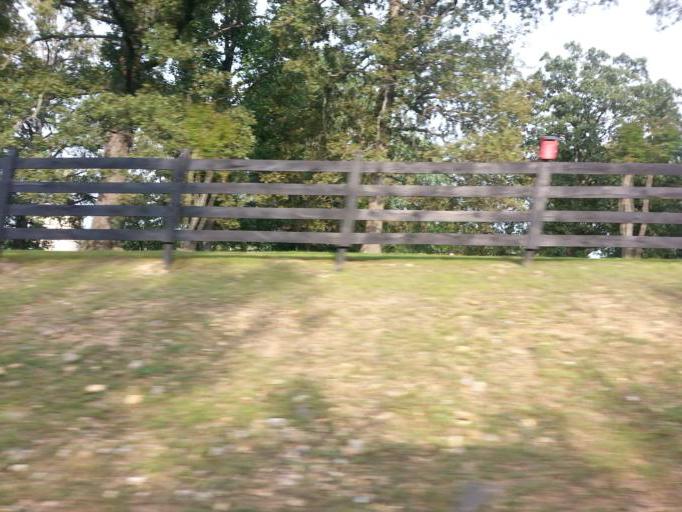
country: US
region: Tennessee
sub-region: Dickson County
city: Burns
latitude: 36.0221
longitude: -87.3324
